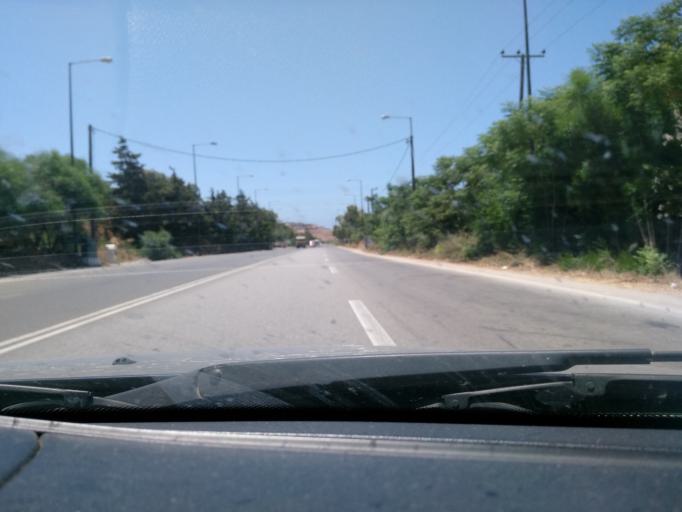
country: GR
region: Crete
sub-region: Nomos Rethymnis
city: Panormos
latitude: 35.4151
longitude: 24.6964
